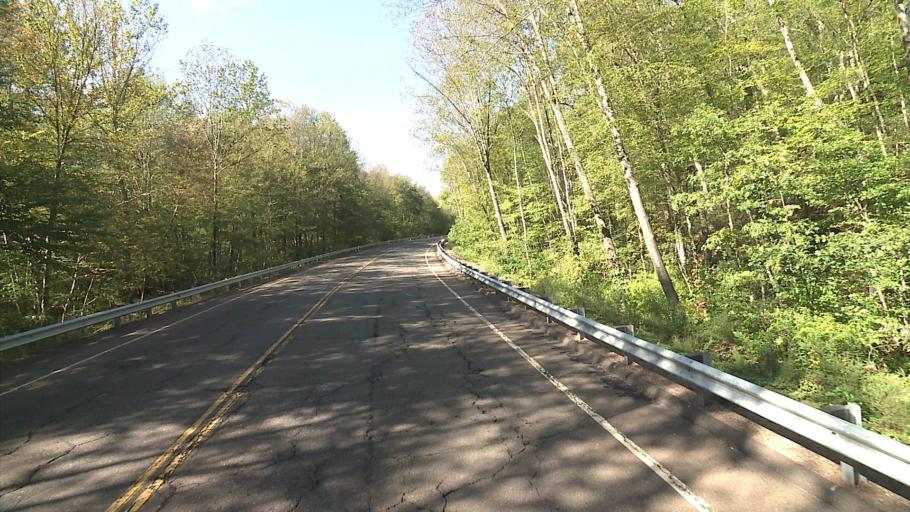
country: US
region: Connecticut
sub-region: Middlesex County
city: Higganum
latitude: 41.5148
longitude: -72.5757
